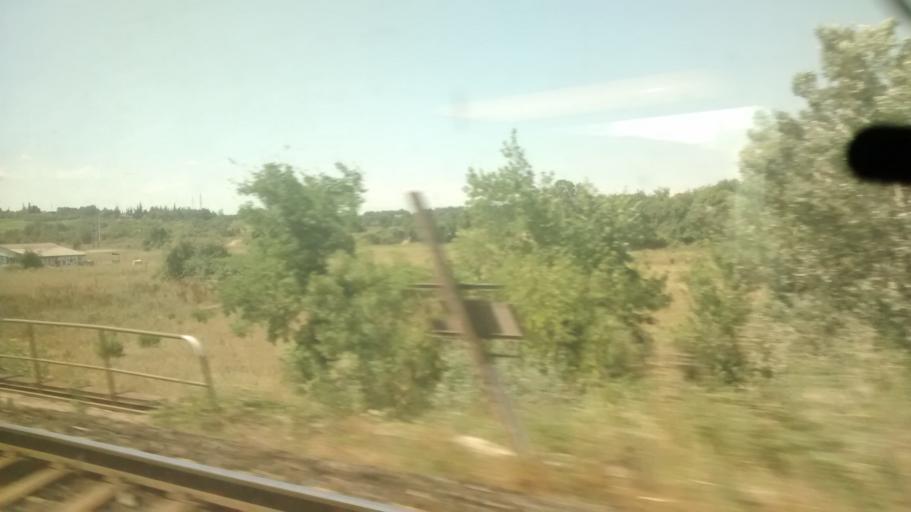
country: FR
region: Languedoc-Roussillon
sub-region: Departement de l'Herault
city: Lunel-Viel
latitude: 43.6820
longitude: 4.1005
